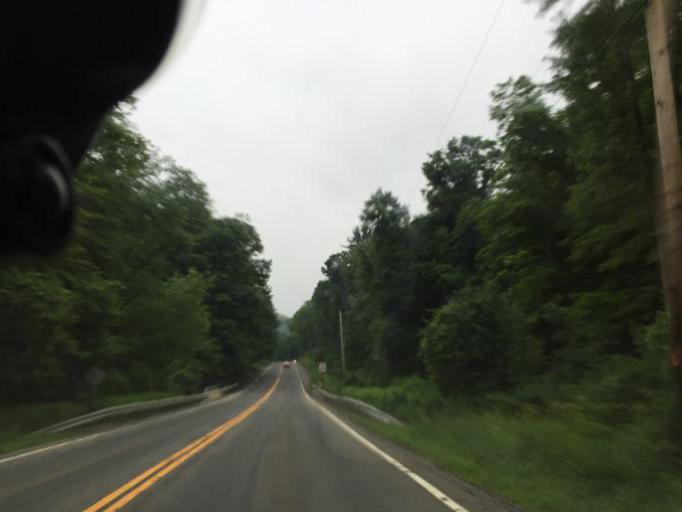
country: US
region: Connecticut
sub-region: Litchfield County
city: Canaan
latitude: 41.9270
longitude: -73.2804
